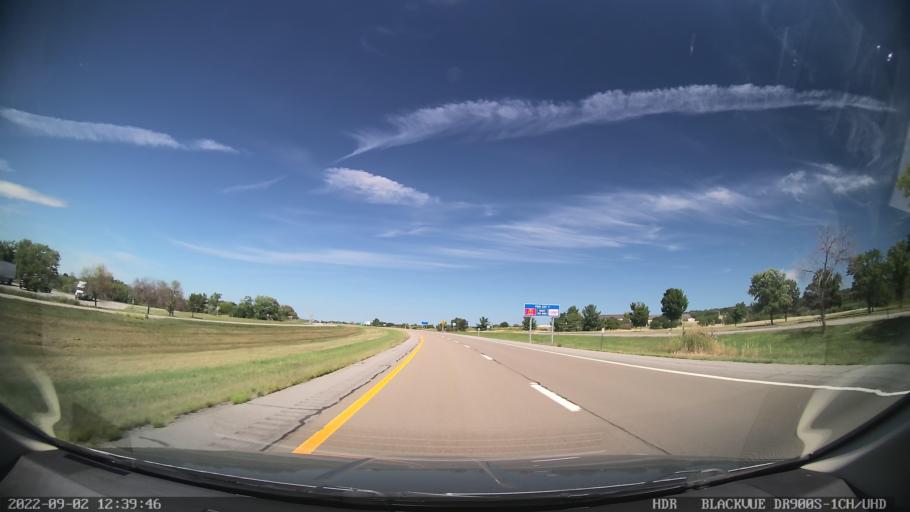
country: US
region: New York
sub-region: Livingston County
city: Mount Morris
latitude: 42.7274
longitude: -77.8306
